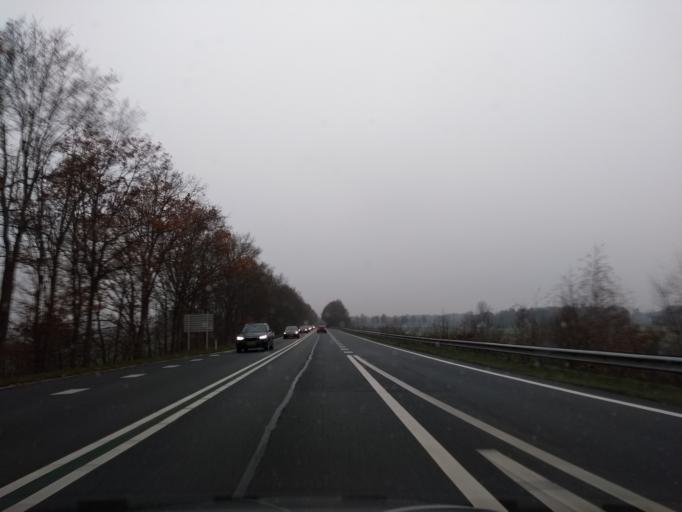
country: NL
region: Overijssel
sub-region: Gemeente Twenterand
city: Vroomshoop
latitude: 52.4997
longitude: 6.5781
